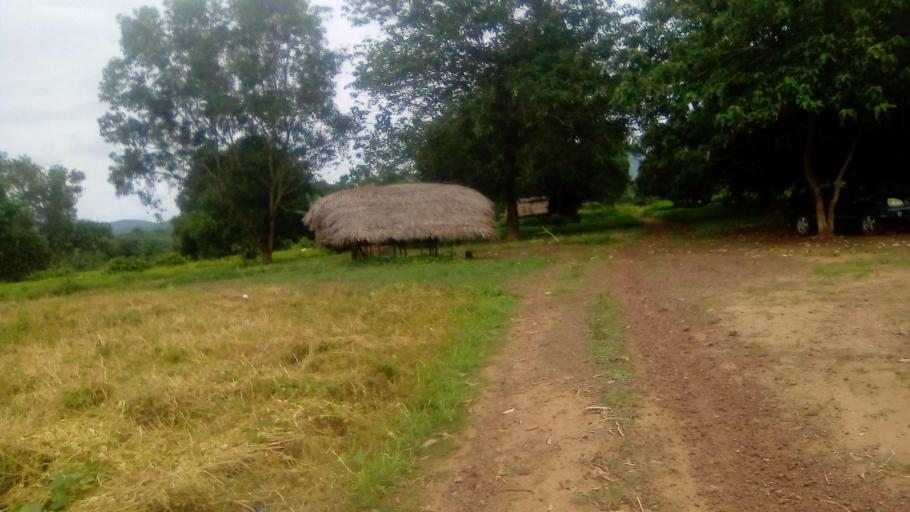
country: SL
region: Southern Province
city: Moyamba
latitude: 8.1562
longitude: -12.4210
